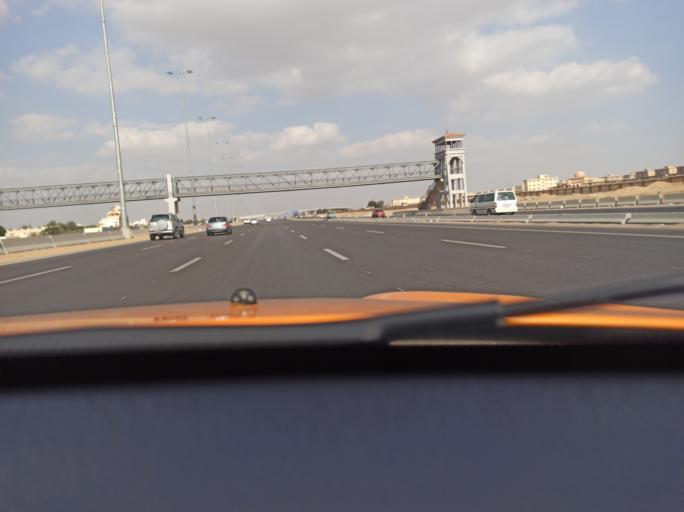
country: EG
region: Muhafazat al Qalyubiyah
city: Al Khankah
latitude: 30.1717
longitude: 31.5346
